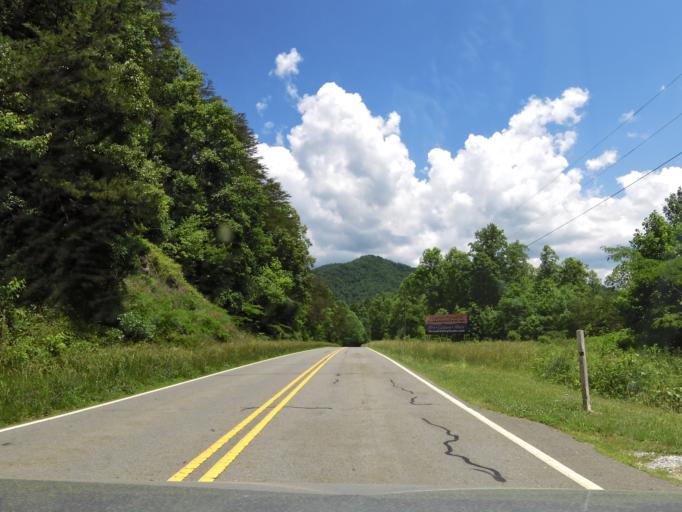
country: US
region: North Carolina
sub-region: Graham County
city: Robbinsville
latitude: 35.3573
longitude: -83.8363
